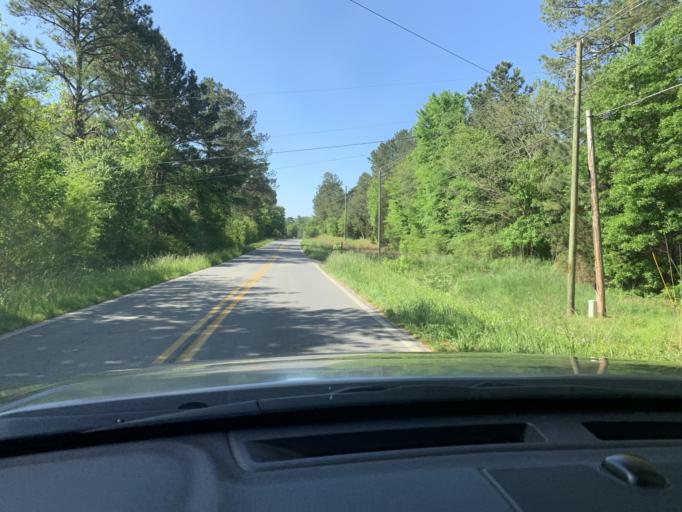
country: US
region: Georgia
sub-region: Polk County
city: Cedartown
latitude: 34.0298
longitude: -85.3001
